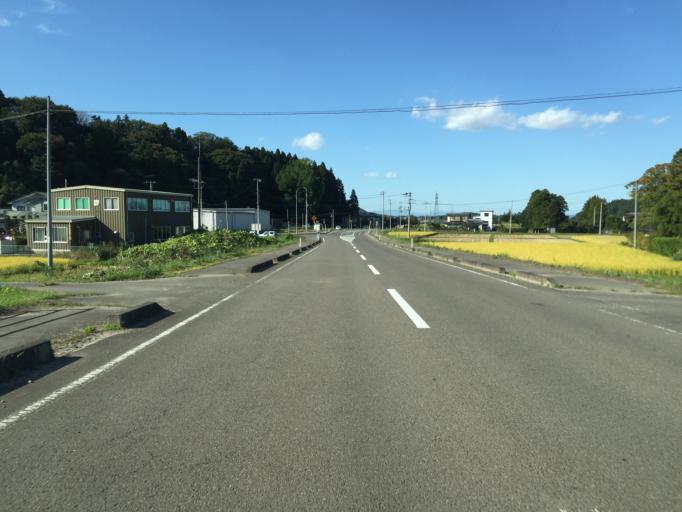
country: JP
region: Miyagi
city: Marumori
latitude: 37.8967
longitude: 140.7699
